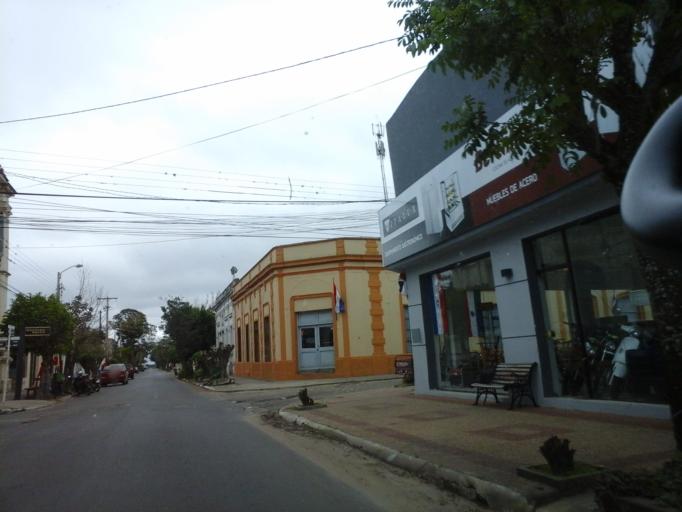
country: PY
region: Neembucu
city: Pilar
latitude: -26.8556
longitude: -58.3072
